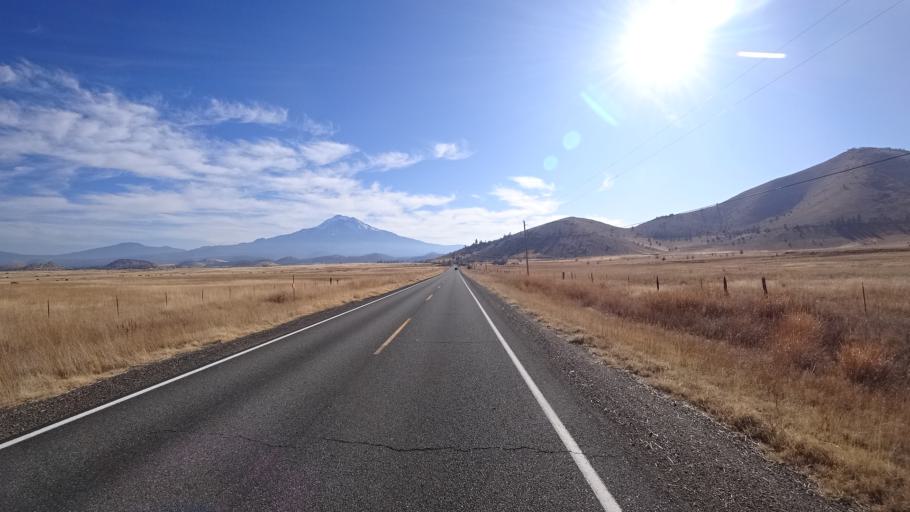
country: US
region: California
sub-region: Siskiyou County
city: Weed
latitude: 41.4734
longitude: -122.4813
